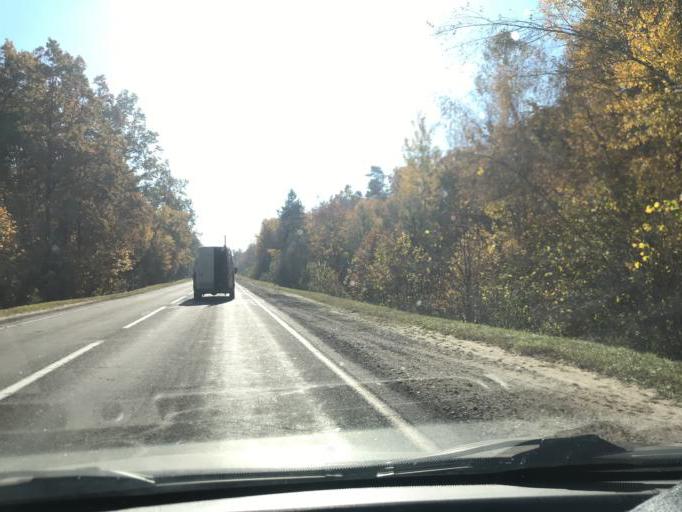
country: BY
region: Gomel
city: Gomel
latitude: 52.4104
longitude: 30.8288
